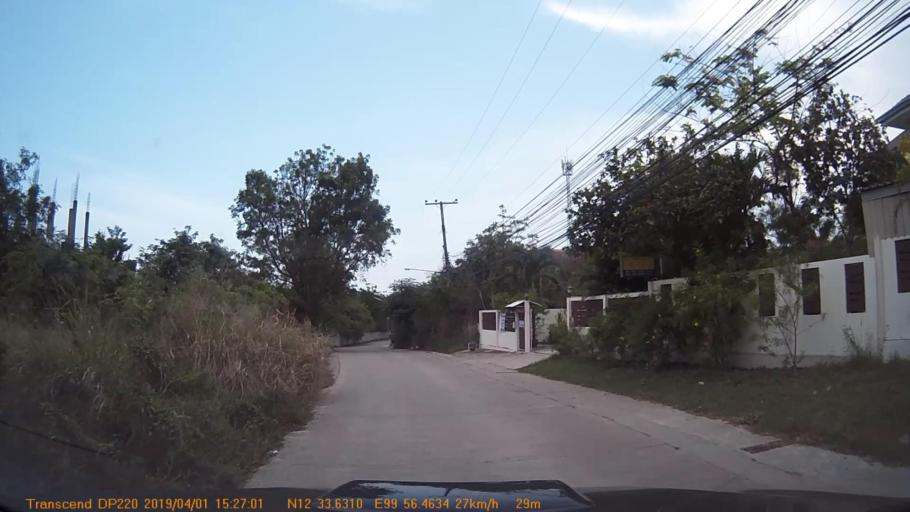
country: TH
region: Prachuap Khiri Khan
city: Hua Hin
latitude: 12.5603
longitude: 99.9412
